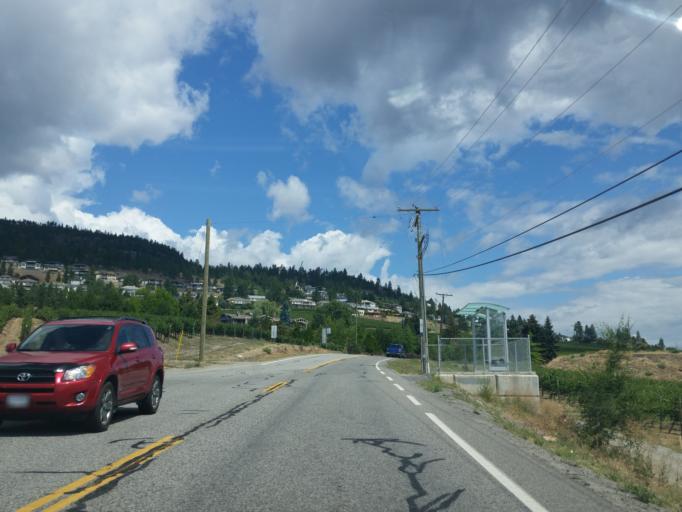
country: CA
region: British Columbia
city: West Kelowna
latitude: 49.8399
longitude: -119.5739
